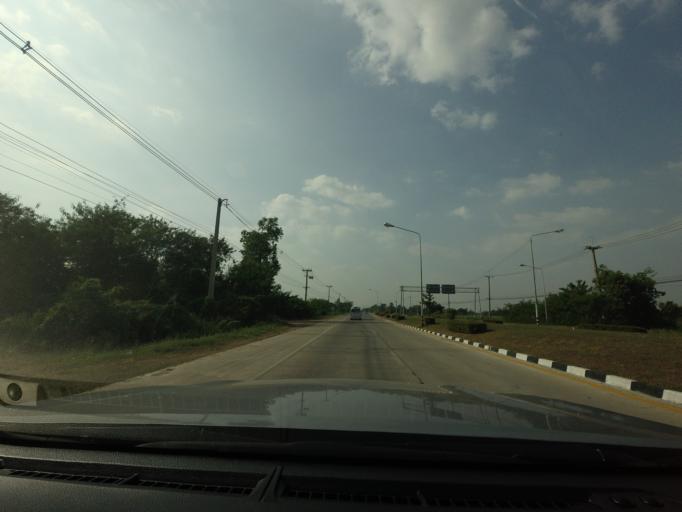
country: TH
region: Sukhothai
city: Kong Krailat
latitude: 17.0078
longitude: 99.9275
